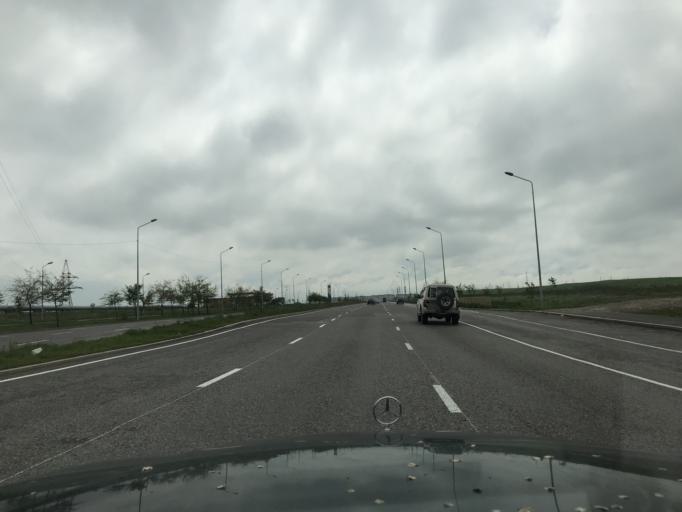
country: KZ
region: Almaty Oblysy
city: Burunday
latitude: 43.2978
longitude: 76.8340
